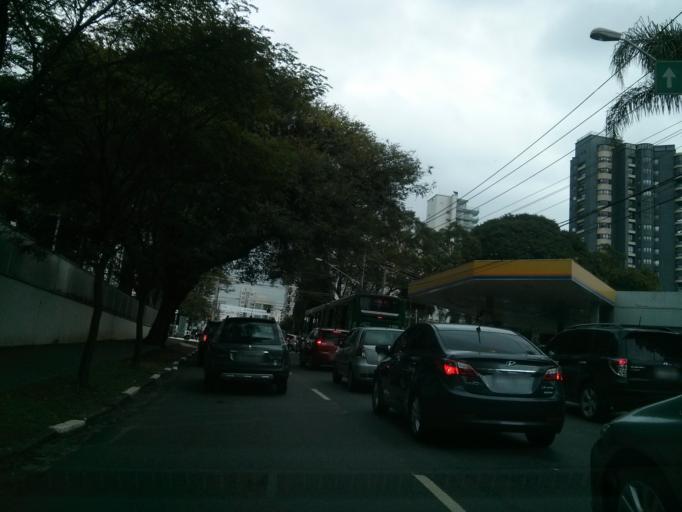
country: BR
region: Sao Paulo
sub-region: Sao Paulo
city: Sao Paulo
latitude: -23.6017
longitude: -46.6558
